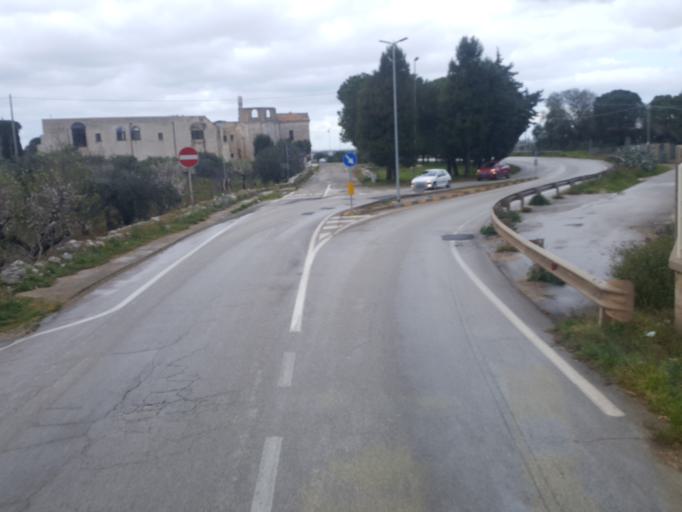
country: IT
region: Apulia
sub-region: Provincia di Bari
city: Conversano
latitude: 40.9780
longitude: 17.1000
